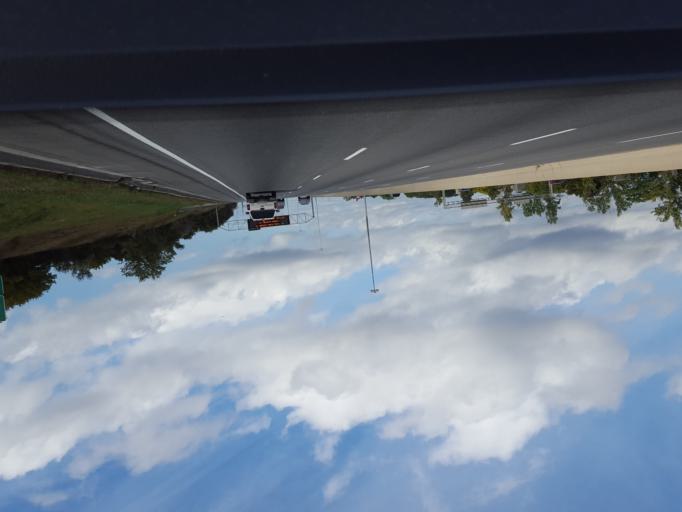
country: CA
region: Ontario
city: Scarborough
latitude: 43.7937
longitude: -79.2137
